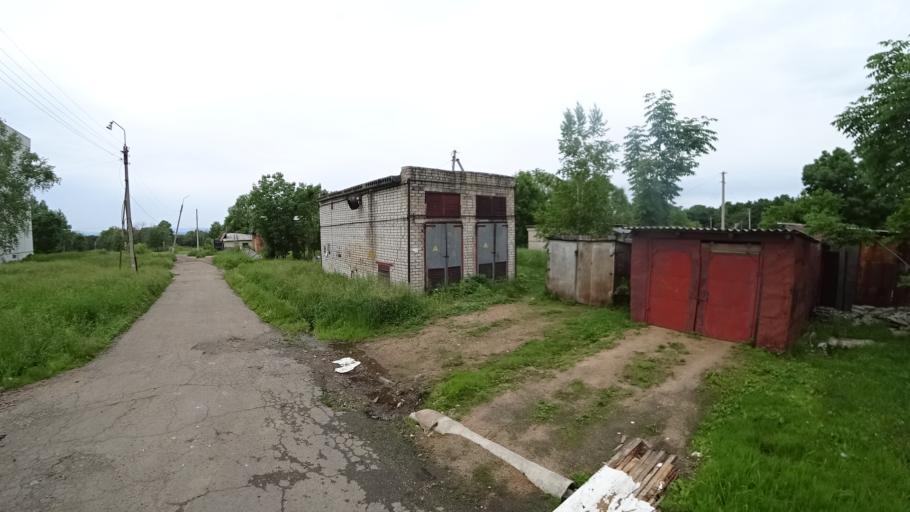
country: RU
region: Primorskiy
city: Novosysoyevka
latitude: 44.1824
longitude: 133.3519
